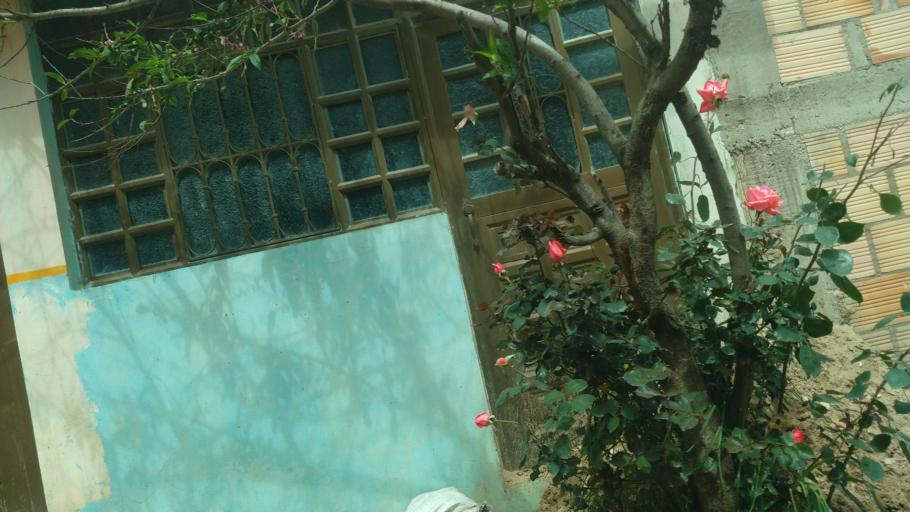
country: CO
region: Cundinamarca
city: Soacha
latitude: 4.5777
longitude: -74.1817
